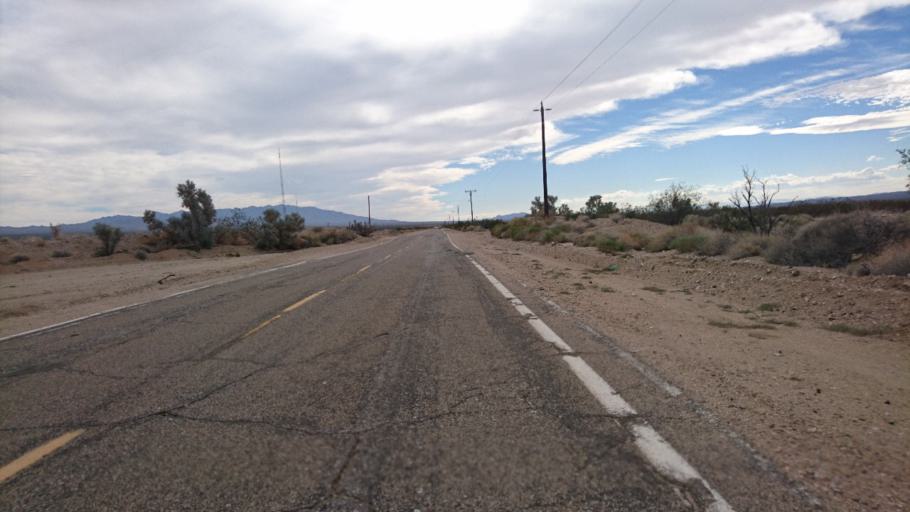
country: US
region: California
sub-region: San Bernardino County
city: Needles
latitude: 34.7698
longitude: -115.2129
